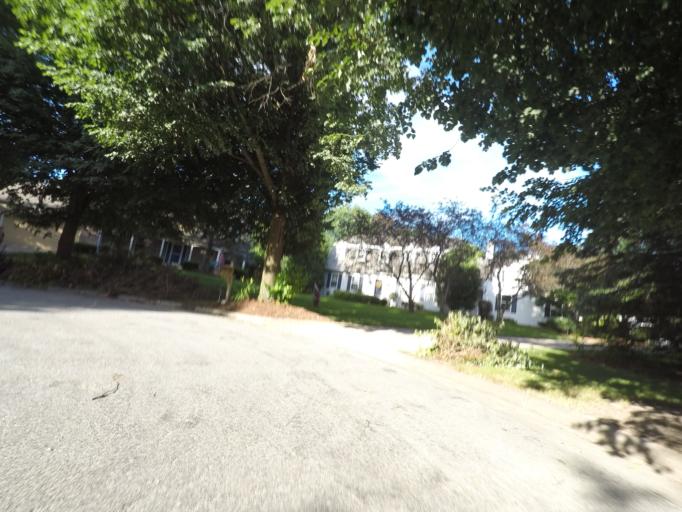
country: US
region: Wisconsin
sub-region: Dane County
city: Middleton
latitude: 43.0732
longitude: -89.5153
